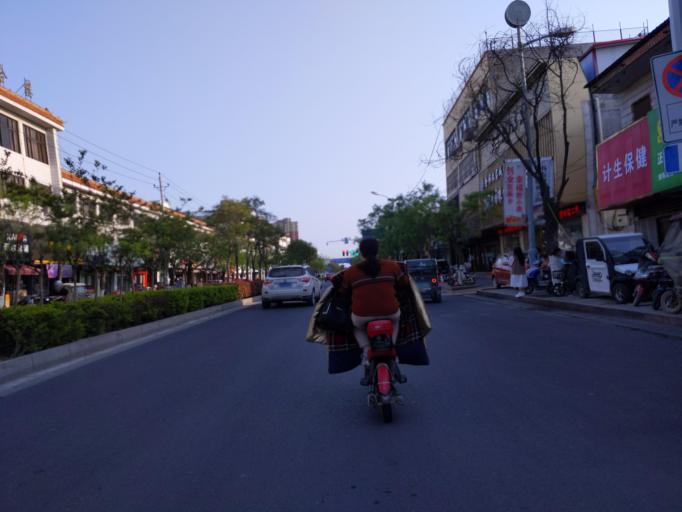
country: CN
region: Henan Sheng
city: Puyang Chengguanzhen
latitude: 35.7021
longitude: 115.0162
